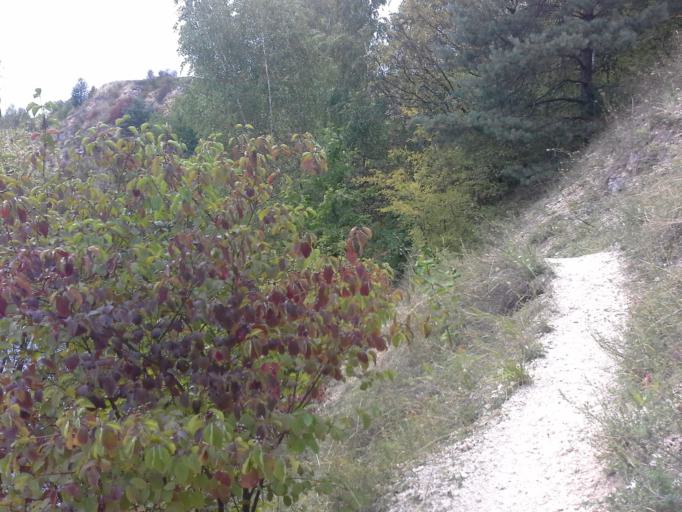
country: PL
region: Lesser Poland Voivodeship
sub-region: Powiat chrzanowski
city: Trzebinia
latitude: 50.1651
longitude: 19.4646
